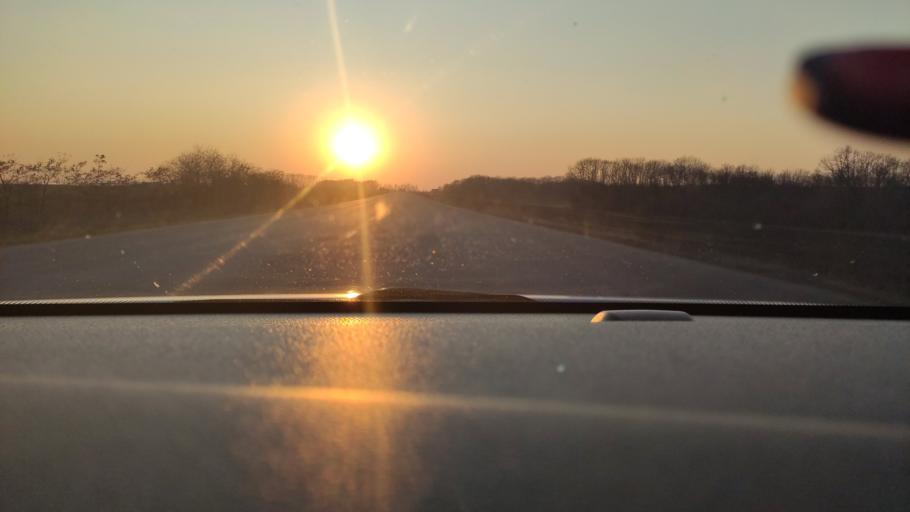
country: RU
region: Voronezj
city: Kolodeznyy
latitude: 51.3397
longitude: 39.0474
